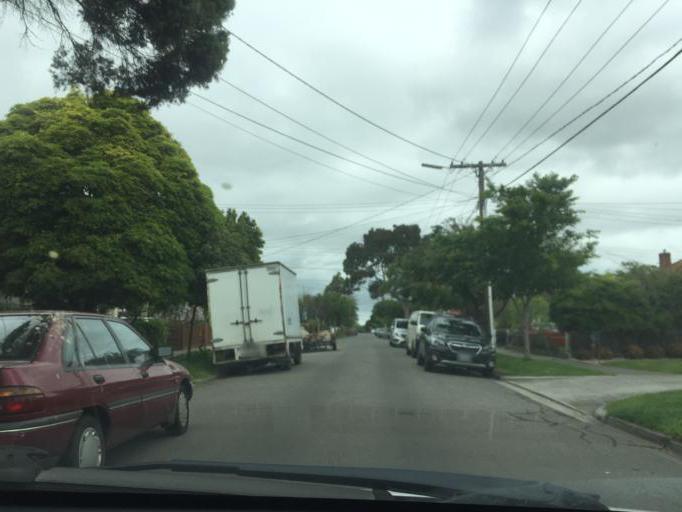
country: AU
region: Victoria
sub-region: Maribyrnong
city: Kingsville
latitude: -37.8139
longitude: 144.8716
